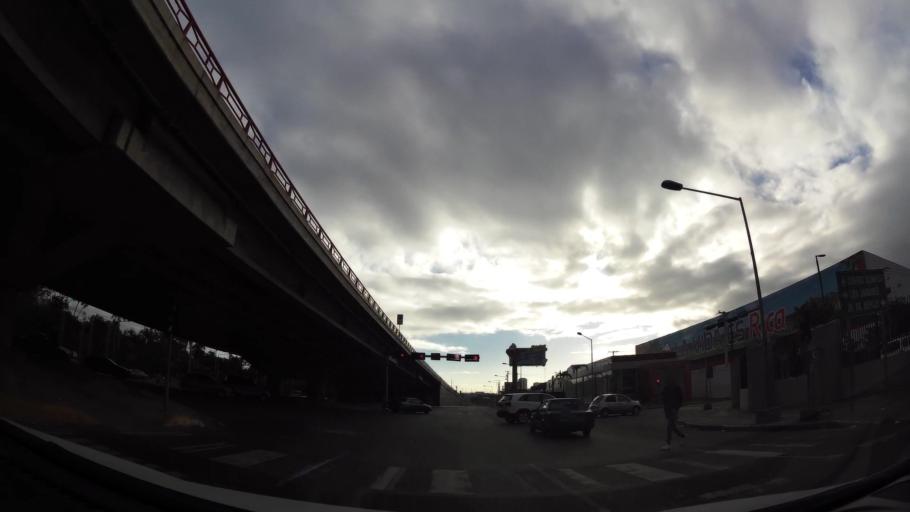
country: DO
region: Nacional
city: La Julia
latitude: 18.4816
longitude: -69.9549
